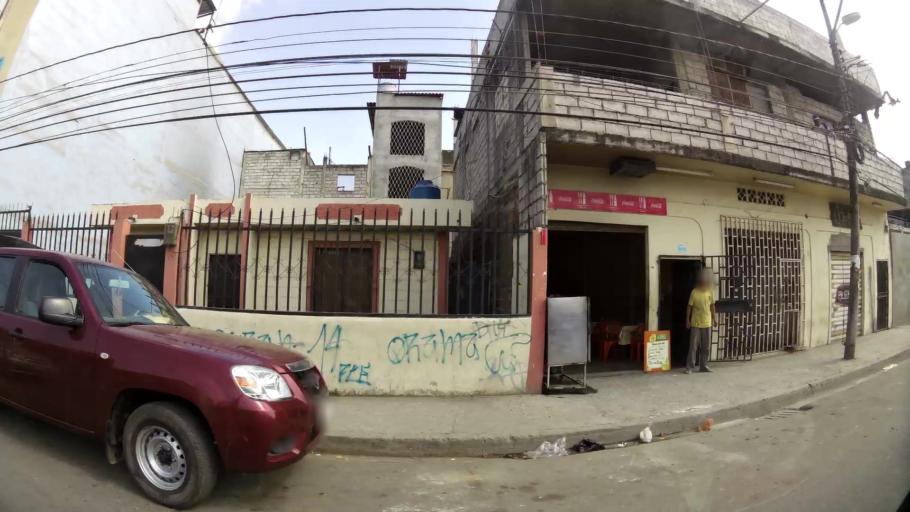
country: EC
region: Guayas
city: Eloy Alfaro
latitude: -2.1748
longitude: -79.8300
